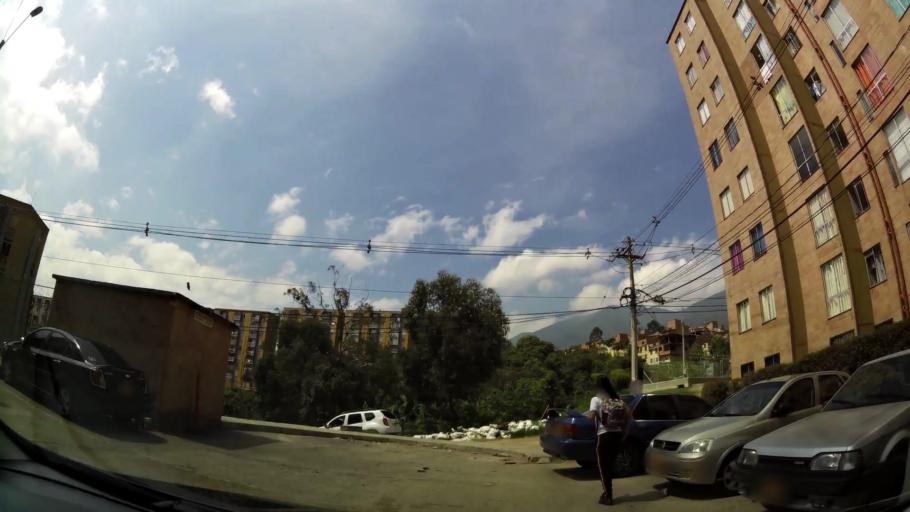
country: CO
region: Antioquia
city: La Estrella
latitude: 6.1746
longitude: -75.6469
